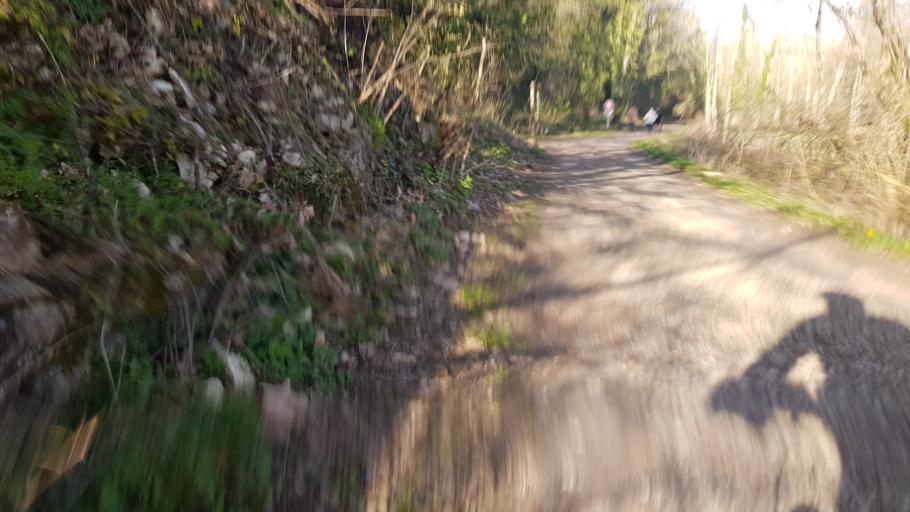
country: FR
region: Poitou-Charentes
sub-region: Departement de la Vienne
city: Migne-Auxances
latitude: 46.6274
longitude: 0.3207
